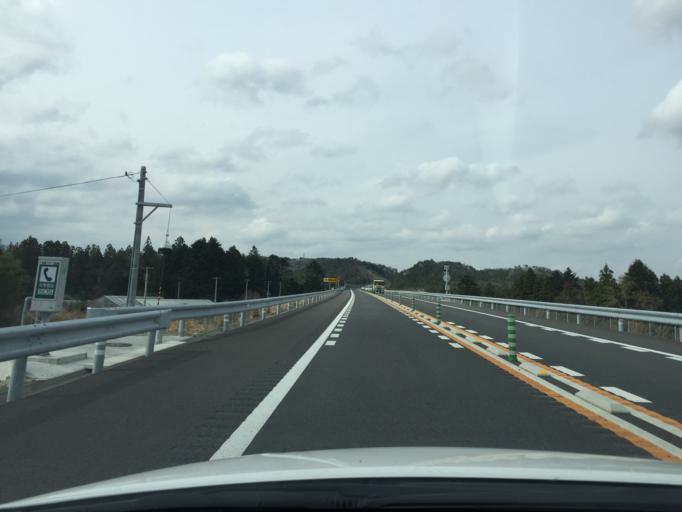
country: JP
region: Fukushima
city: Namie
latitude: 37.4284
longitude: 140.9610
